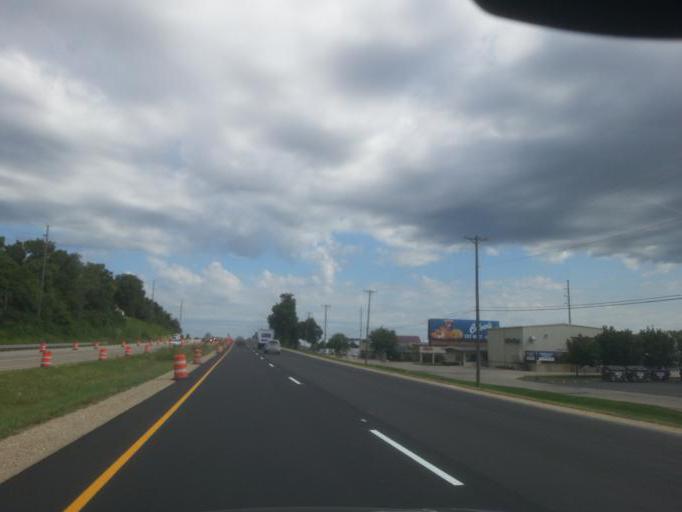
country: US
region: Wisconsin
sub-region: Dane County
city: Monona
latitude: 43.0781
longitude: -89.3102
